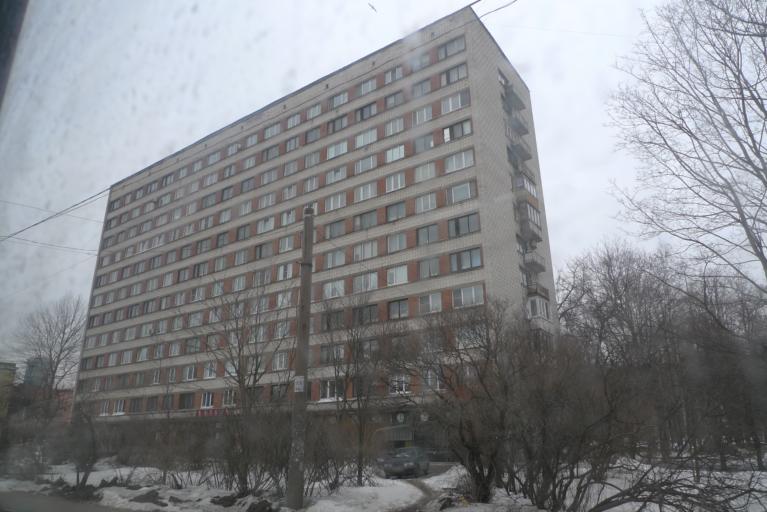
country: RU
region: Leningrad
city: Udel'naya
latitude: 60.0197
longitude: 30.3212
